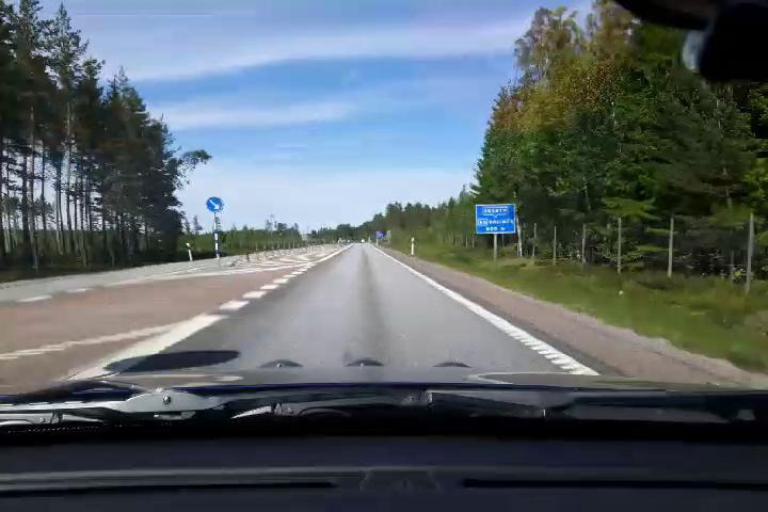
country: SE
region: Gaevleborg
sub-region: Gavle Kommun
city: Norrsundet
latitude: 61.0598
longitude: 16.9620
